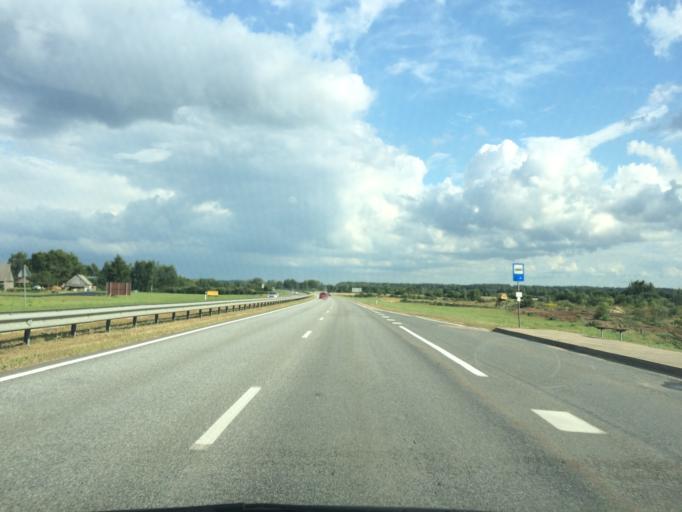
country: LV
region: Ikskile
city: Ikskile
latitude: 56.8227
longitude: 24.5356
